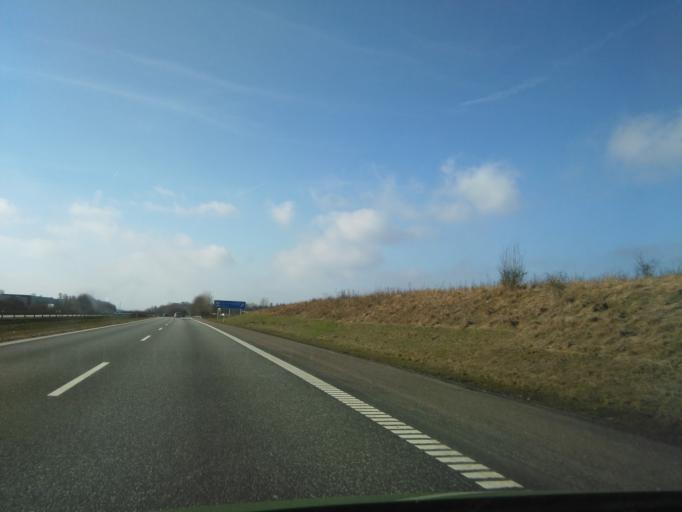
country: DK
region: Central Jutland
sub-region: Skanderborg Kommune
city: Stilling
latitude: 56.0704
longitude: 9.9860
